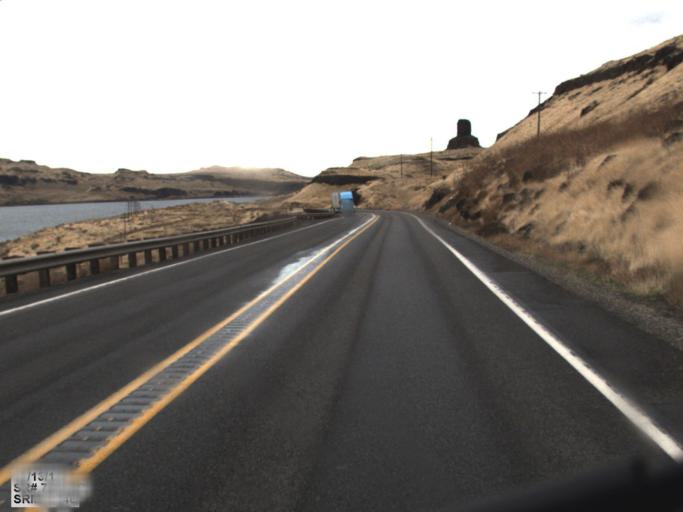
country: US
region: Washington
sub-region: Benton County
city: Finley
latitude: 46.0359
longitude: -118.9364
